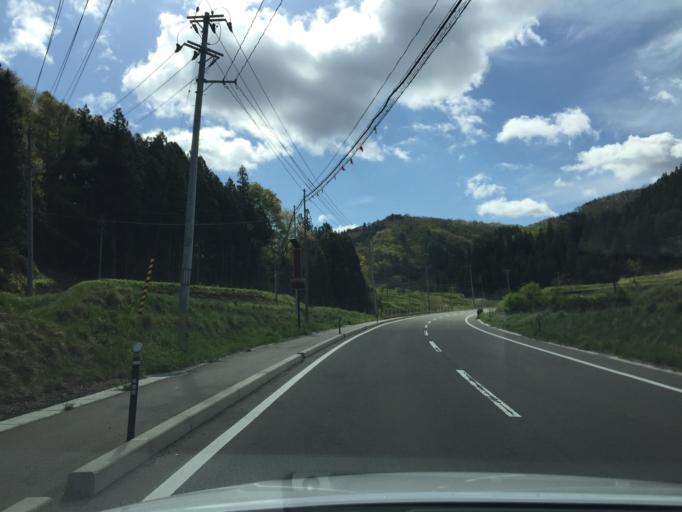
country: JP
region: Fukushima
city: Hobaramachi
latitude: 37.6404
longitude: 140.6419
